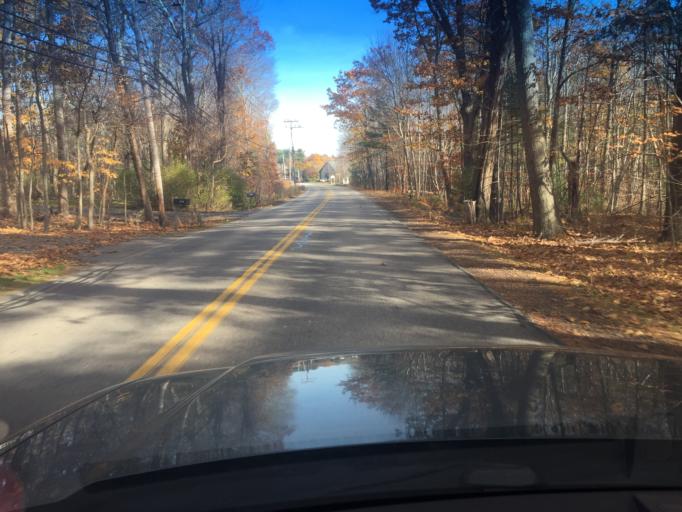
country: US
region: Maine
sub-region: York County
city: York Harbor
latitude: 43.1577
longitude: -70.6314
